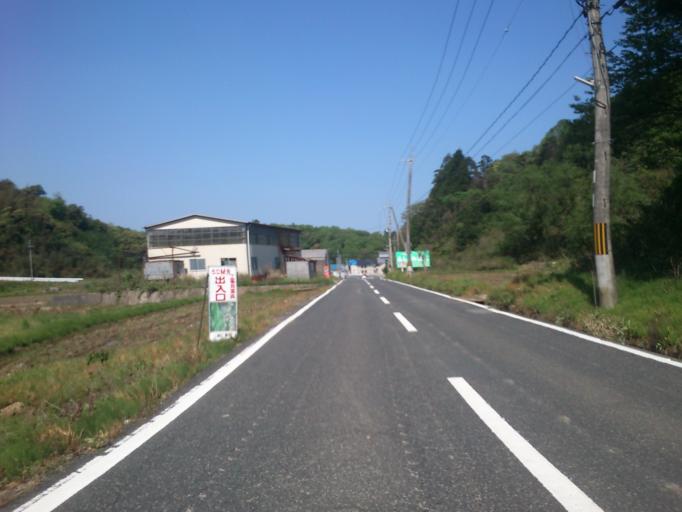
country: JP
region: Kyoto
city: Miyazu
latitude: 35.6840
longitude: 135.0624
